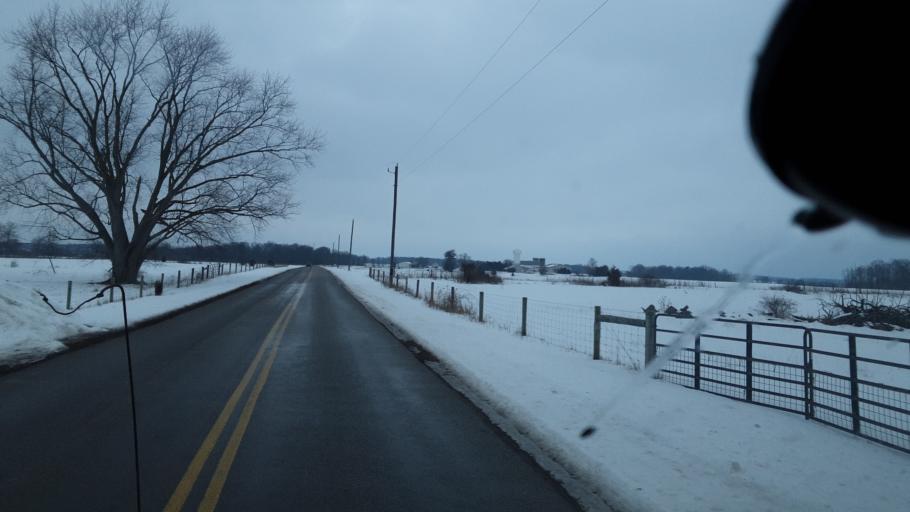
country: US
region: Ohio
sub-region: Union County
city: New California
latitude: 40.1825
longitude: -83.3064
